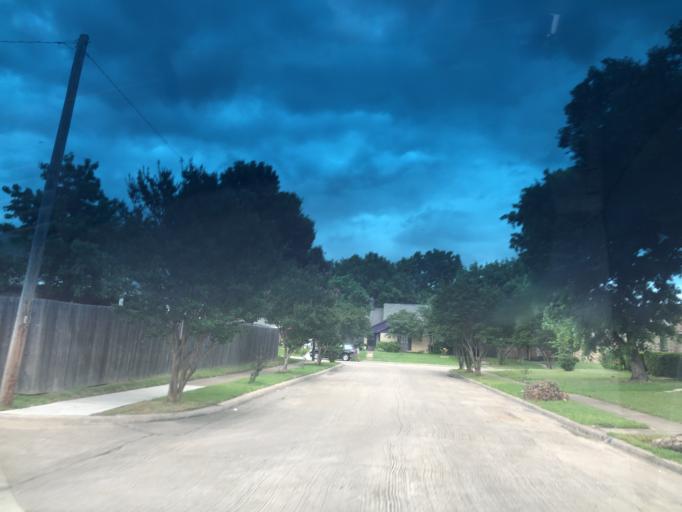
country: US
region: Texas
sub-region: Dallas County
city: Grand Prairie
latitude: 32.6998
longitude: -97.0037
